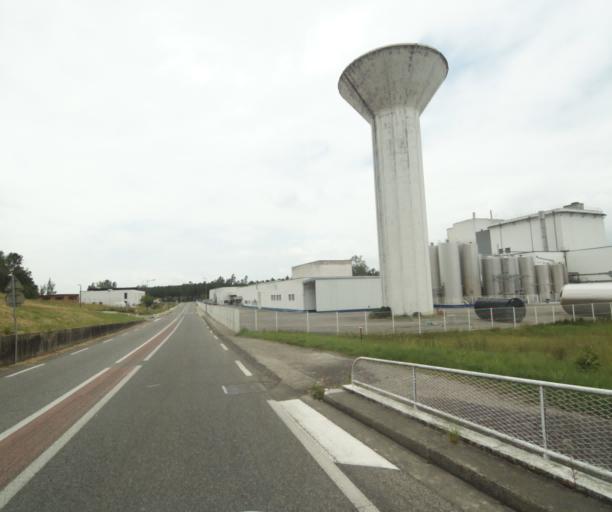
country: FR
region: Midi-Pyrenees
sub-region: Departement du Tarn-et-Garonne
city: Montauban
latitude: 44.0010
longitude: 1.3626
